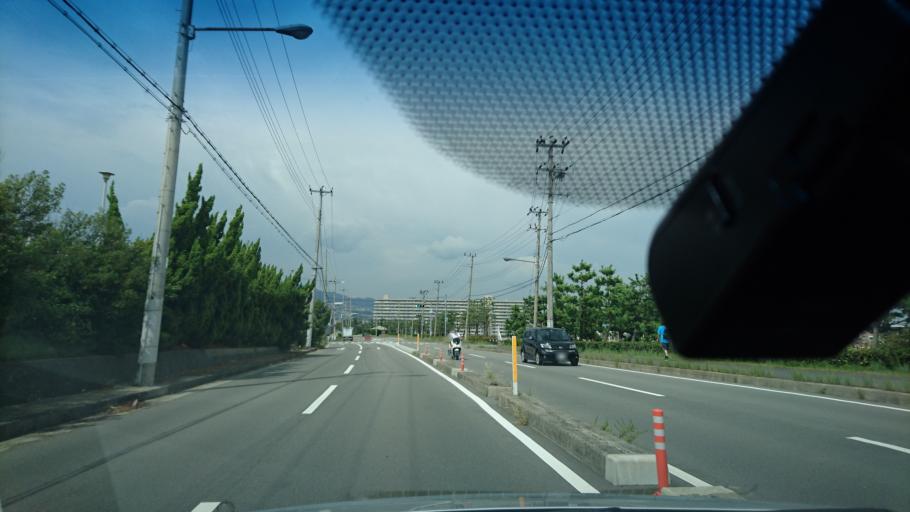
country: JP
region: Hyogo
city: Nishinomiya-hama
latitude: 34.7217
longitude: 135.3236
